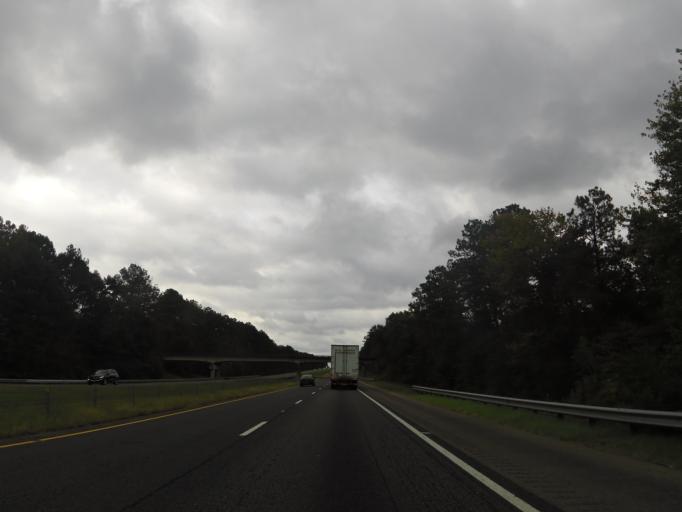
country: US
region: Alabama
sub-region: Butler County
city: Georgiana
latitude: 31.6250
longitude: -86.8012
